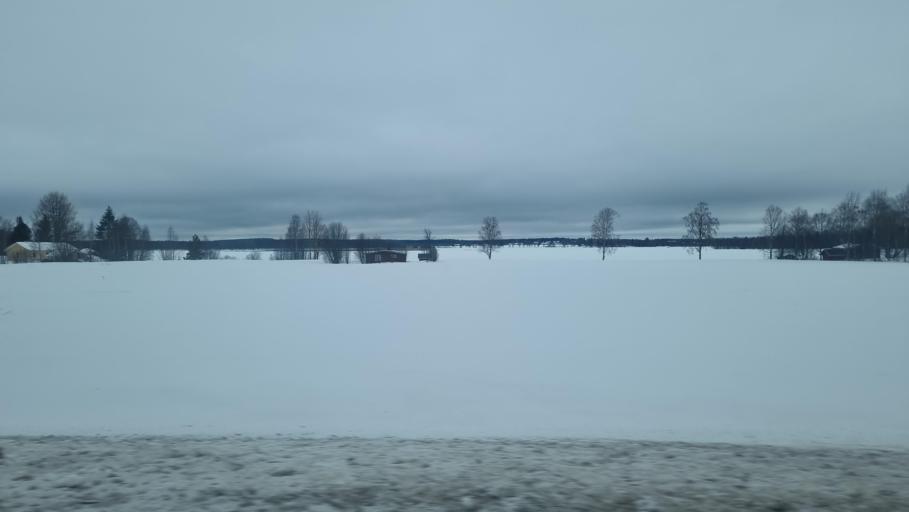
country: FI
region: Lapland
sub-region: Kemi-Tornio
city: Tornio
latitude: 66.0491
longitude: 24.0092
